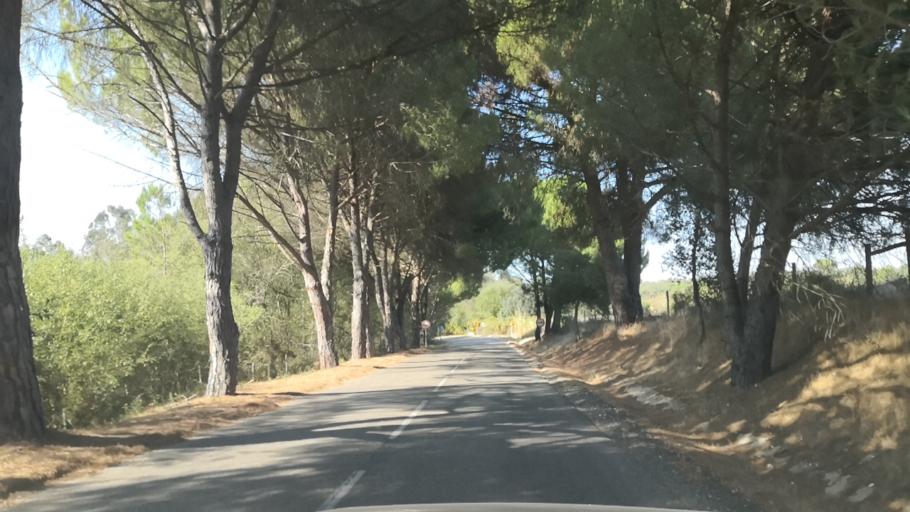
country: PT
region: Santarem
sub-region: Coruche
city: Coruche
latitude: 38.8706
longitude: -8.5385
